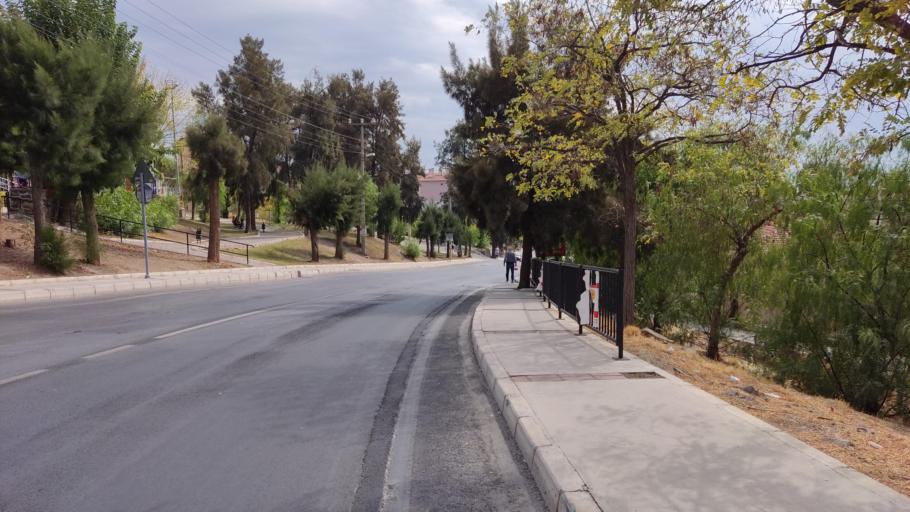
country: TR
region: Izmir
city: Karsiyaka
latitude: 38.4996
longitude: 27.0874
